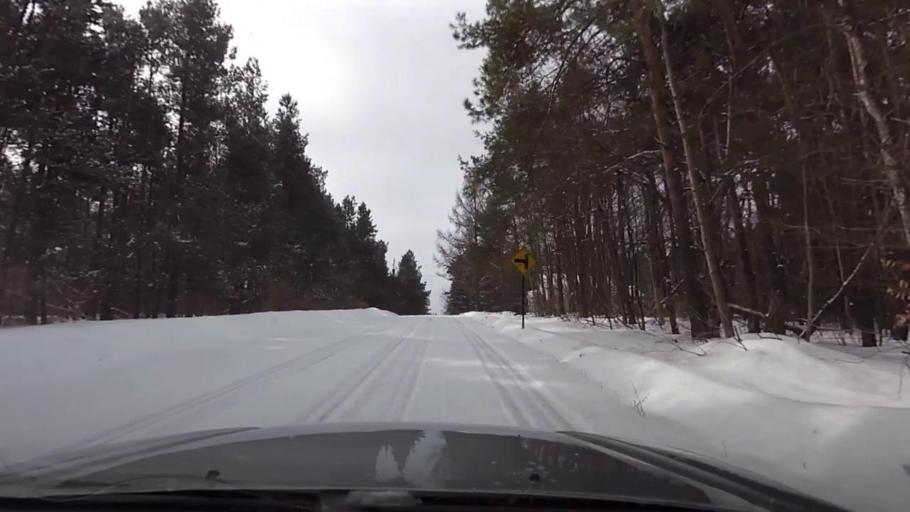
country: US
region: New York
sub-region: Cattaraugus County
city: Franklinville
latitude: 42.3316
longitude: -78.3540
